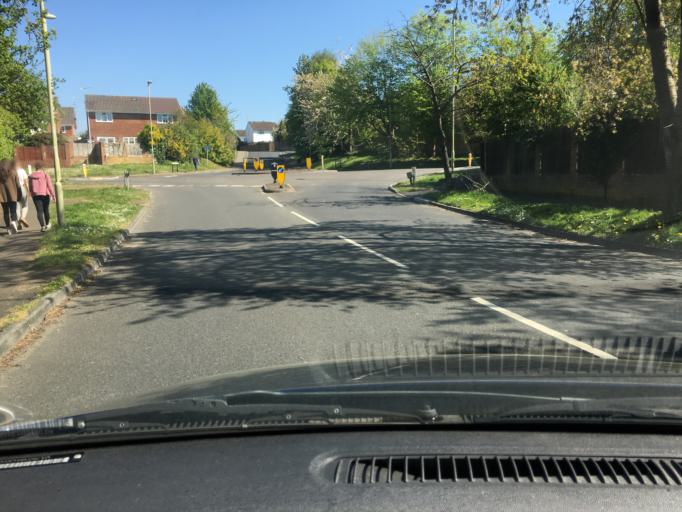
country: GB
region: England
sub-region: Hampshire
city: Yateley
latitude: 51.3331
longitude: -0.8385
